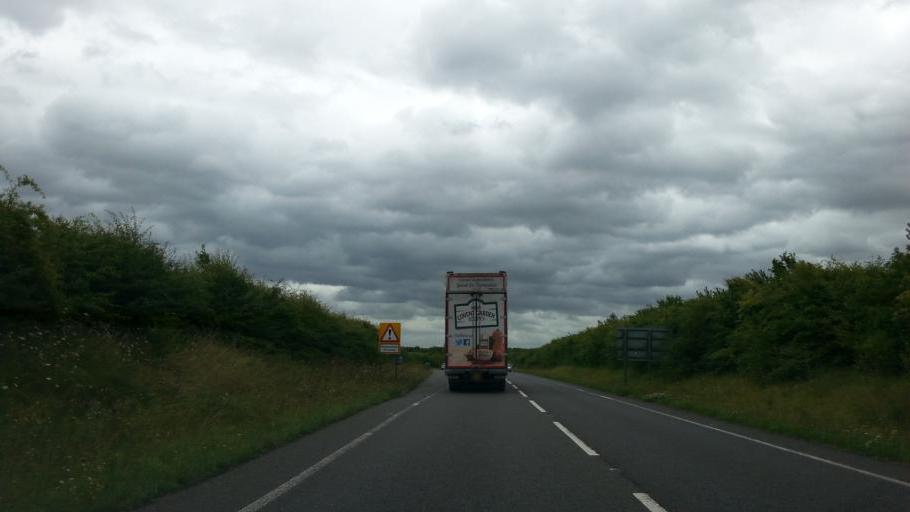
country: GB
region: England
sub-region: Cambridgeshire
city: Papworth Everard
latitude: 52.2172
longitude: -0.0941
